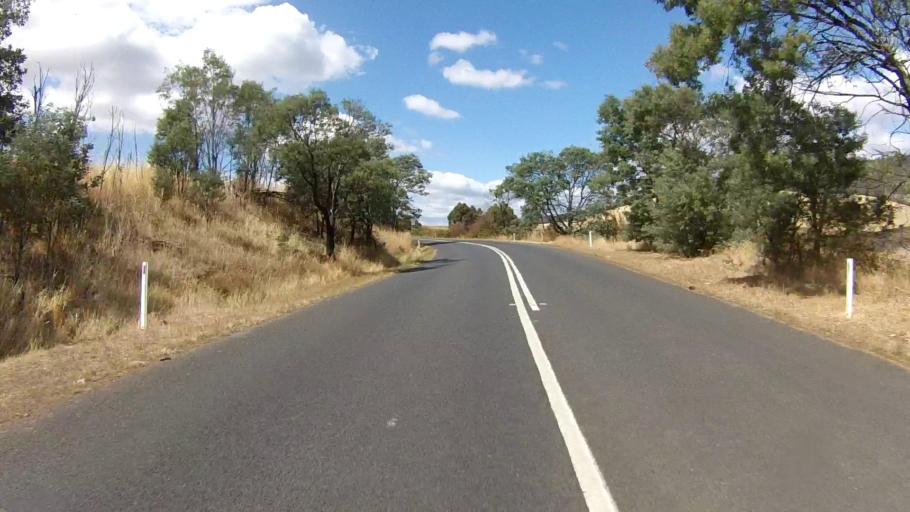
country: AU
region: Tasmania
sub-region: Derwent Valley
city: New Norfolk
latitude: -42.7355
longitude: 146.9285
